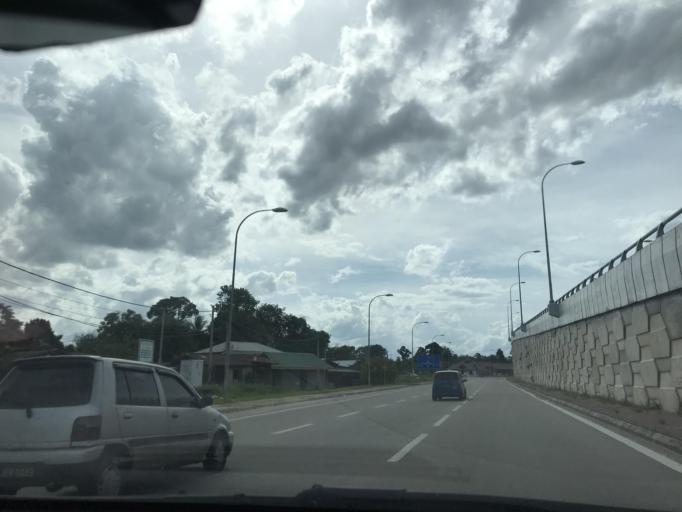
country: MY
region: Kelantan
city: Kampung Lemal
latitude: 6.0283
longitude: 102.1435
